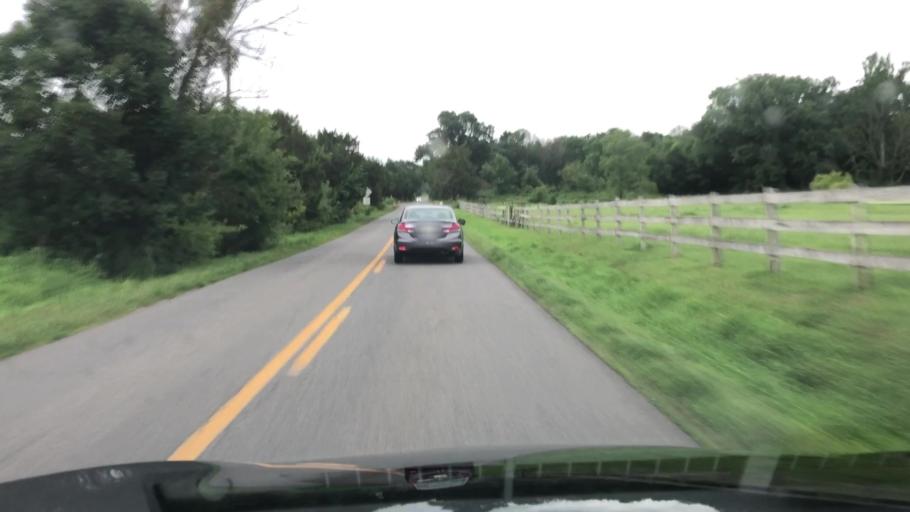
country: US
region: Virginia
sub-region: Prince William County
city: Nokesville
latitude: 38.6777
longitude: -77.6645
